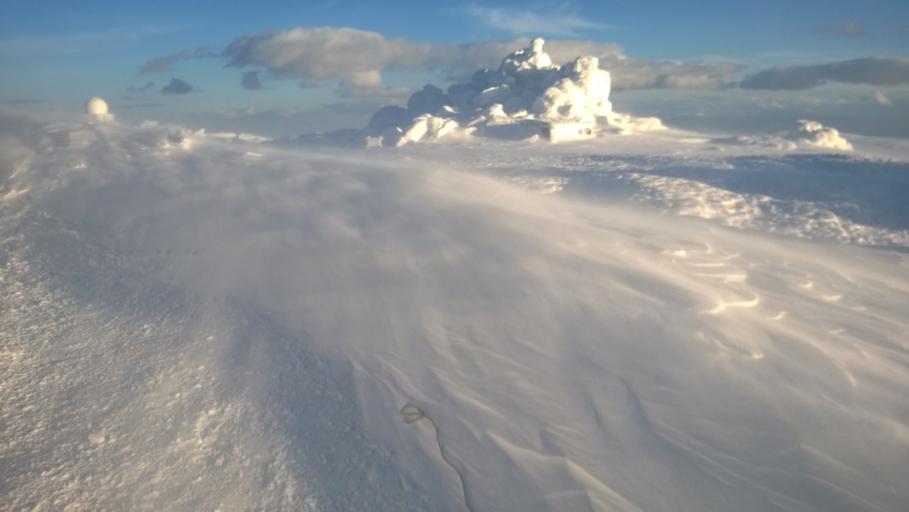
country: BG
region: Sofia-Capital
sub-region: Stolichna Obshtina
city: Sofia
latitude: 42.5636
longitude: 23.2784
